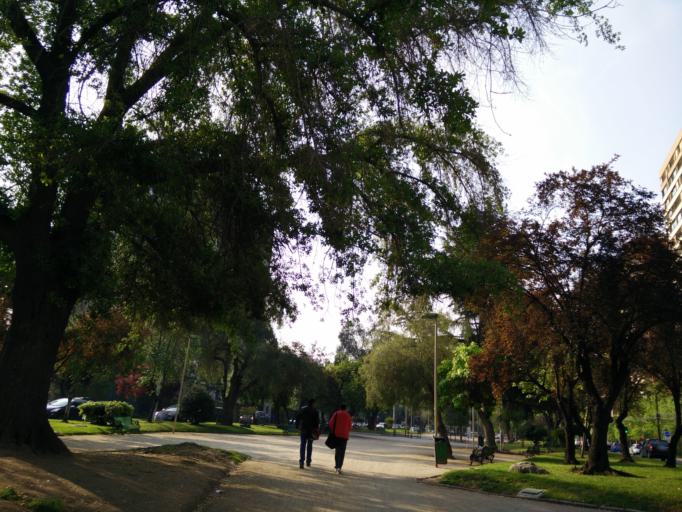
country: CL
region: Santiago Metropolitan
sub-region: Provincia de Santiago
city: Villa Presidente Frei, Nunoa, Santiago, Chile
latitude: -33.4197
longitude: -70.5820
